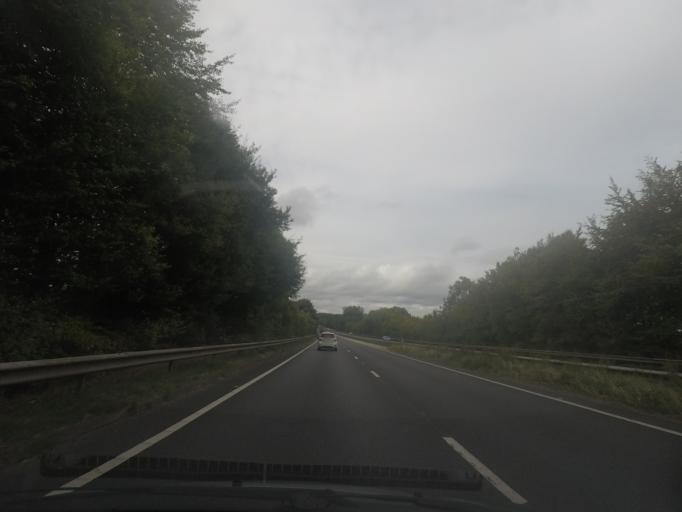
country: GB
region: England
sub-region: Hampshire
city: Overton
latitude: 51.2180
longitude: -1.3424
